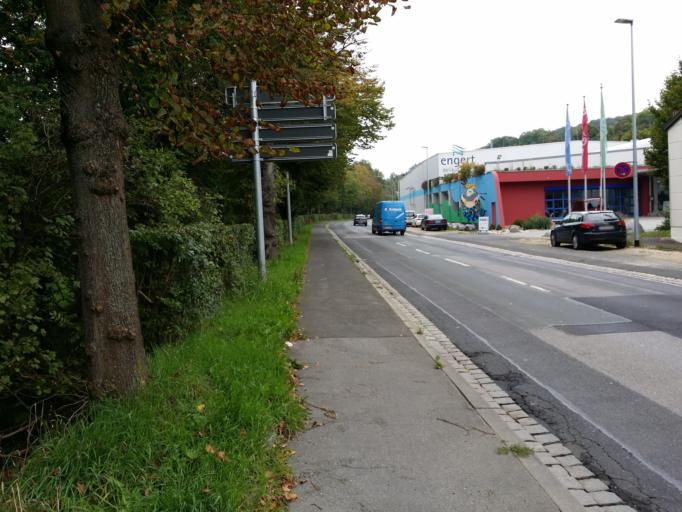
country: DE
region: Bavaria
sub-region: Upper Palatinate
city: Amberg
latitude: 49.4497
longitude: 11.8548
